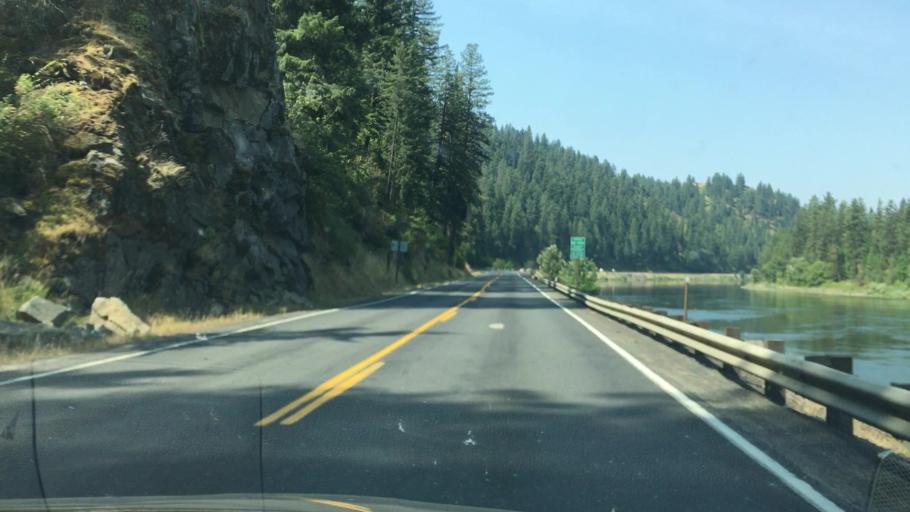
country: US
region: Idaho
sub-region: Clearwater County
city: Orofino
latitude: 46.5002
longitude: -116.3683
